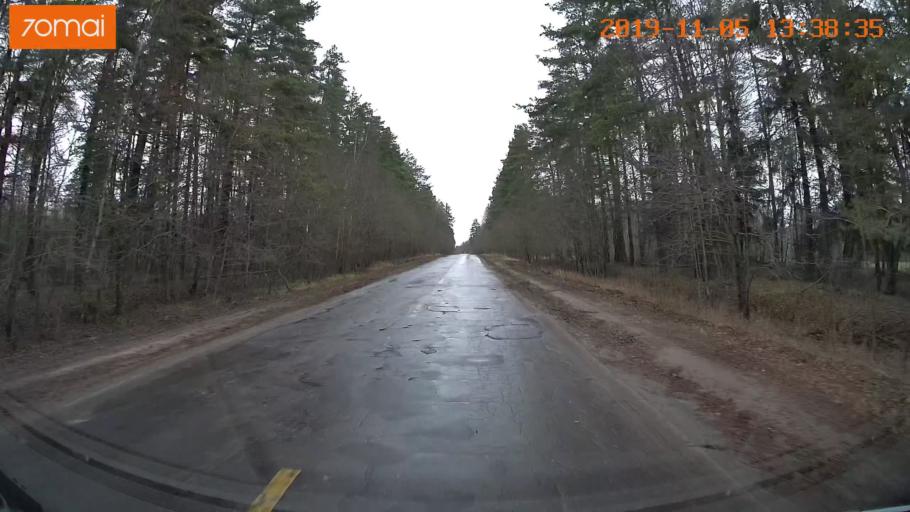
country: RU
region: Ivanovo
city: Shuya
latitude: 56.9330
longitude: 41.3868
